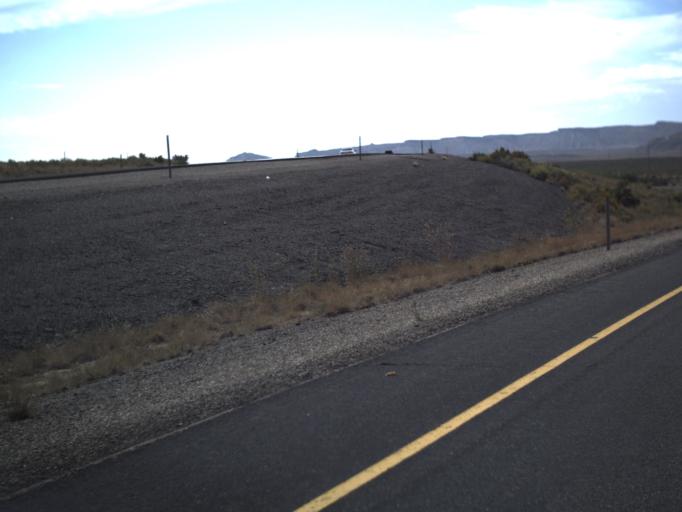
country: US
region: Utah
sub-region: Grand County
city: Moab
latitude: 38.9624
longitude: -109.7188
